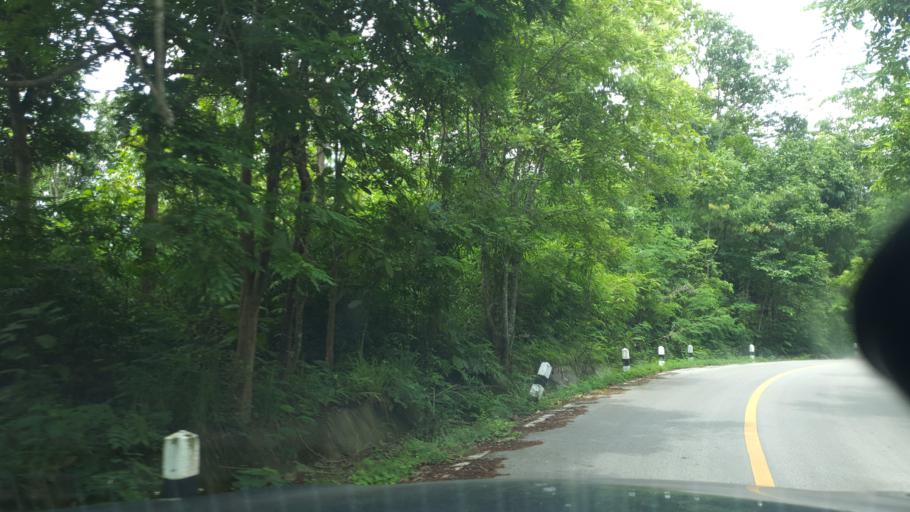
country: TH
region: Lampang
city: Hang Chat
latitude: 18.3875
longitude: 99.2619
